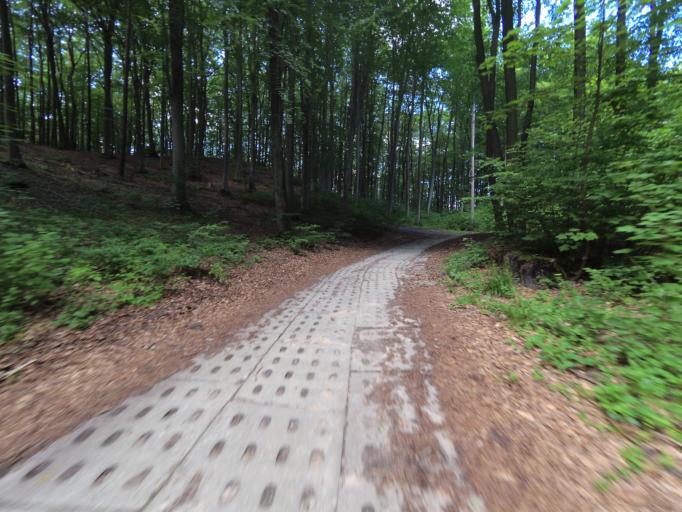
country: PL
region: Pomeranian Voivodeship
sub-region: Gdynia
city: Wielki Kack
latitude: 54.4906
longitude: 18.5061
